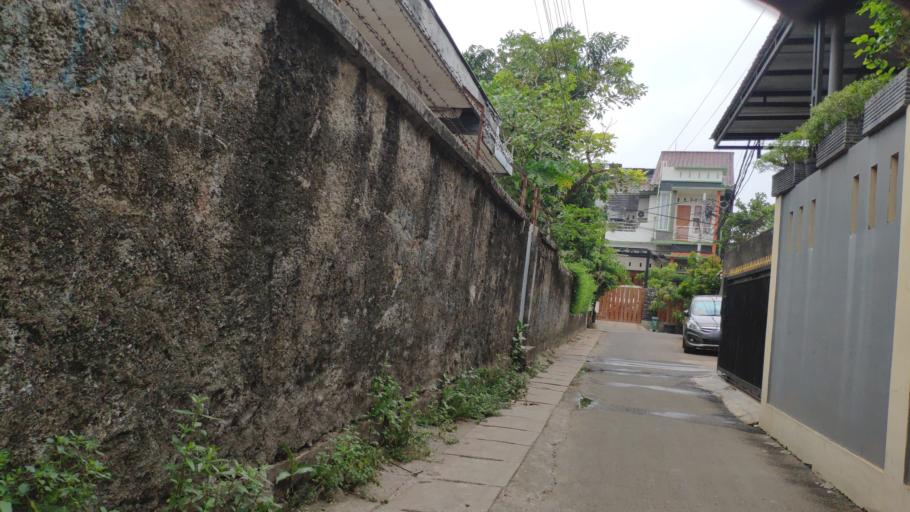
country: ID
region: Jakarta Raya
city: Jakarta
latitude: -6.2630
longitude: 106.7927
